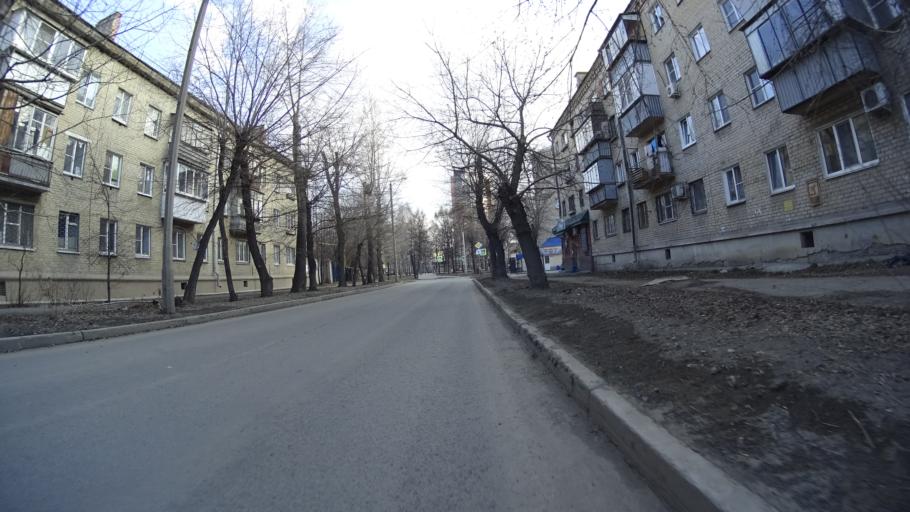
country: RU
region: Chelyabinsk
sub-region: Gorod Chelyabinsk
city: Chelyabinsk
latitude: 55.1449
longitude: 61.3749
